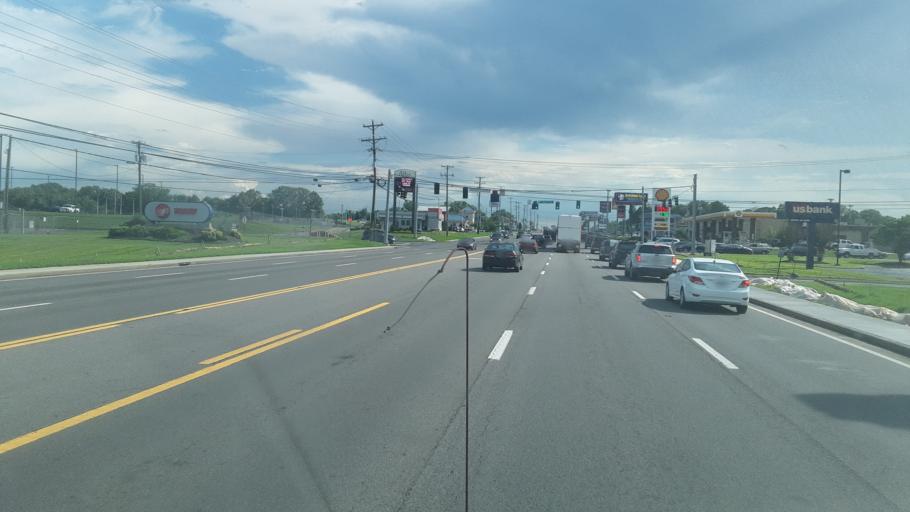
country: US
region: Tennessee
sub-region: Montgomery County
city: Clarksville
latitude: 36.5832
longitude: -87.2968
